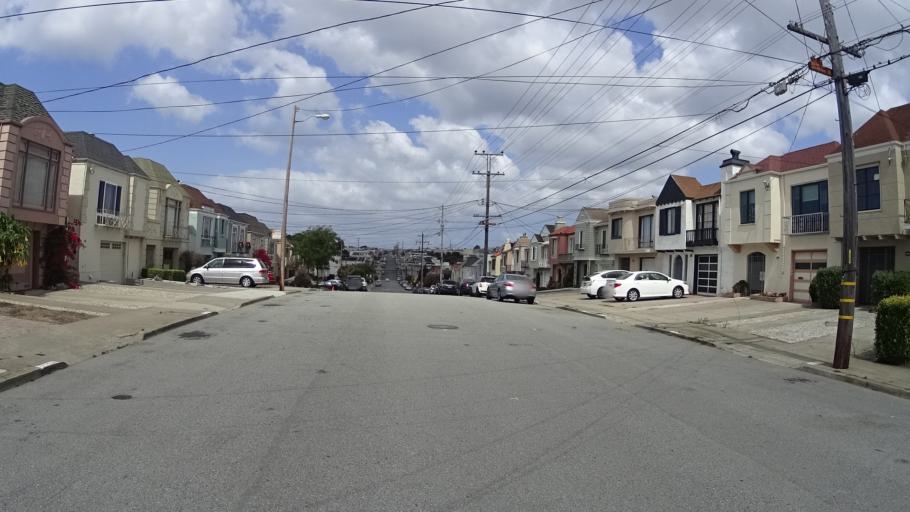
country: US
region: California
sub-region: San Mateo County
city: Daly City
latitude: 37.7358
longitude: -122.4924
